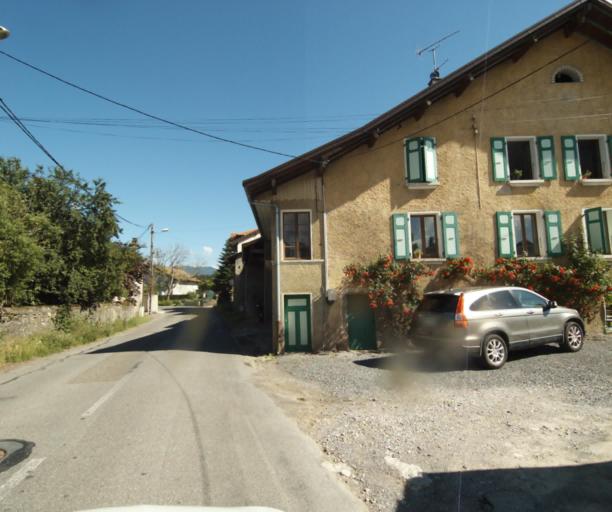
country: FR
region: Rhone-Alpes
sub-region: Departement de la Haute-Savoie
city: Sciez
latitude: 46.3277
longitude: 6.3786
